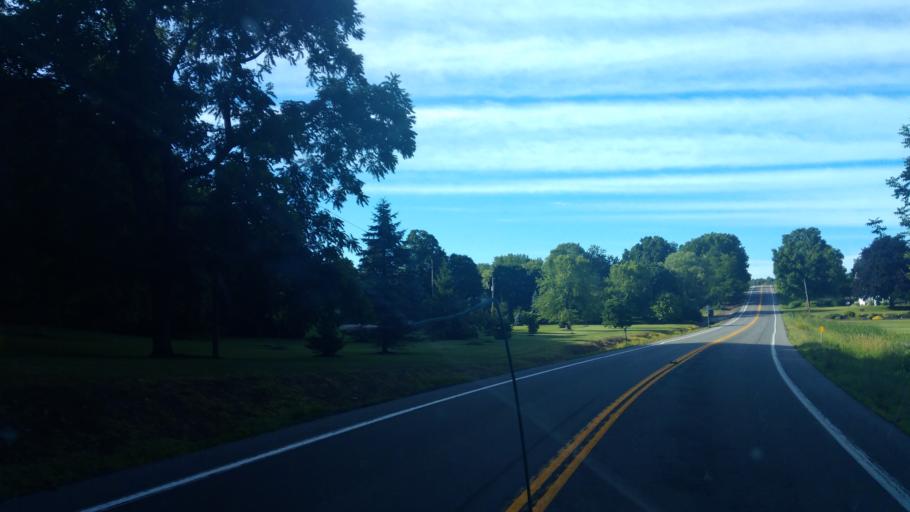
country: US
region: New York
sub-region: Wayne County
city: Lyons
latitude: 43.0900
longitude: -76.9861
